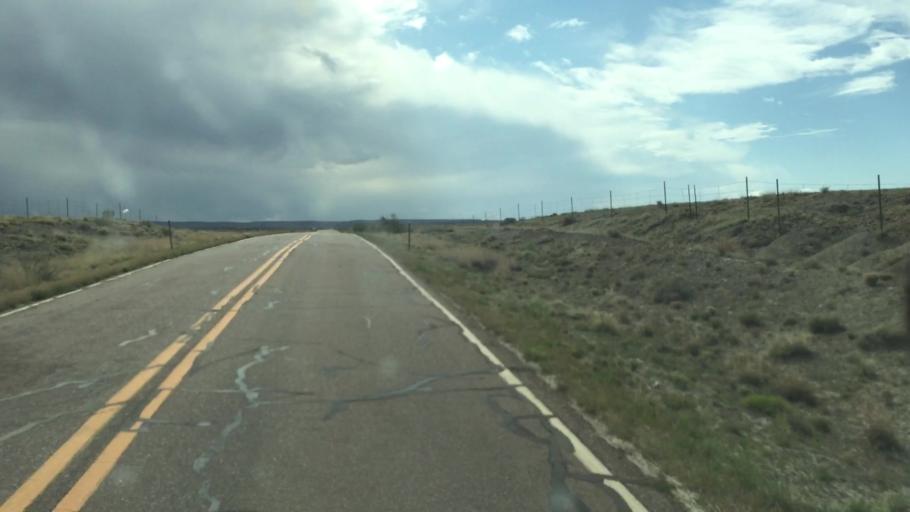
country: US
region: Arizona
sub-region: Navajo County
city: White Mountain Lake
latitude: 34.5174
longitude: -109.7076
